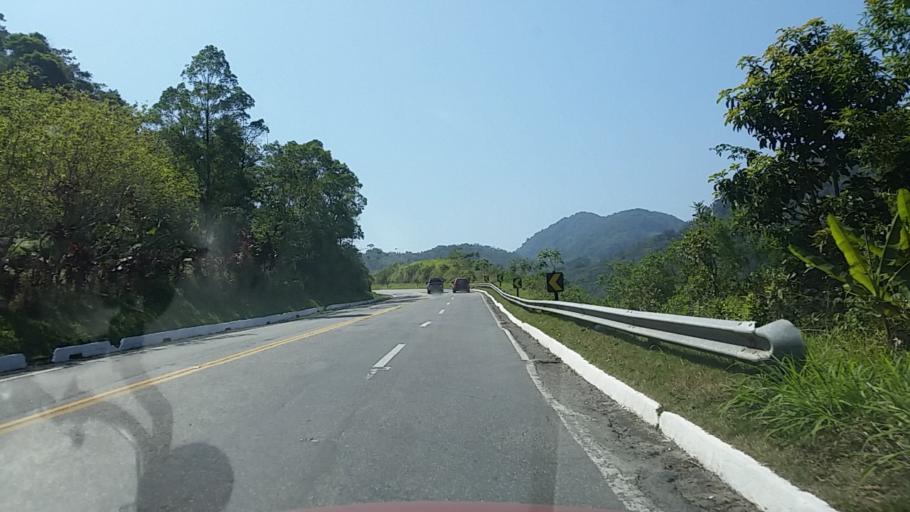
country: BR
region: Sao Paulo
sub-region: Miracatu
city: Miracatu
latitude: -24.3801
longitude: -47.5022
